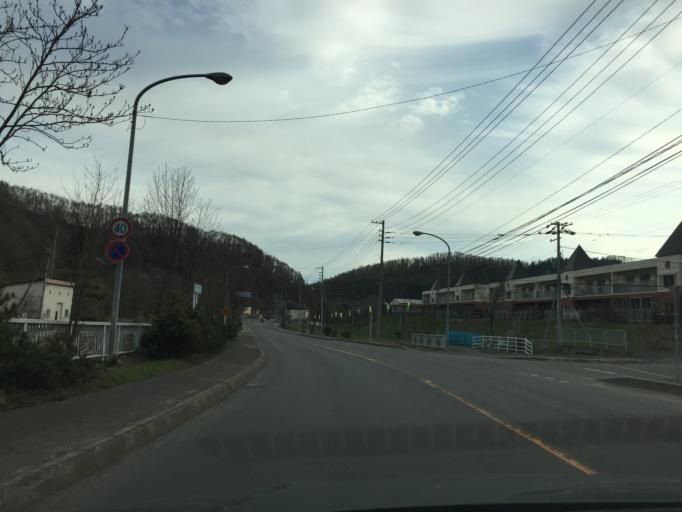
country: JP
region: Hokkaido
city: Utashinai
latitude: 43.5207
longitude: 142.0309
